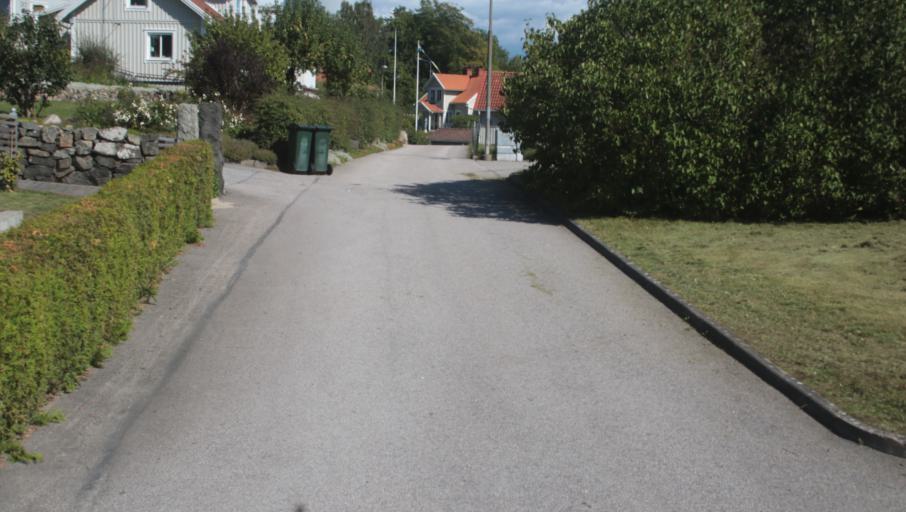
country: SE
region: Blekinge
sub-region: Karlshamns Kommun
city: Karlshamn
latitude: 56.1562
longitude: 14.8540
